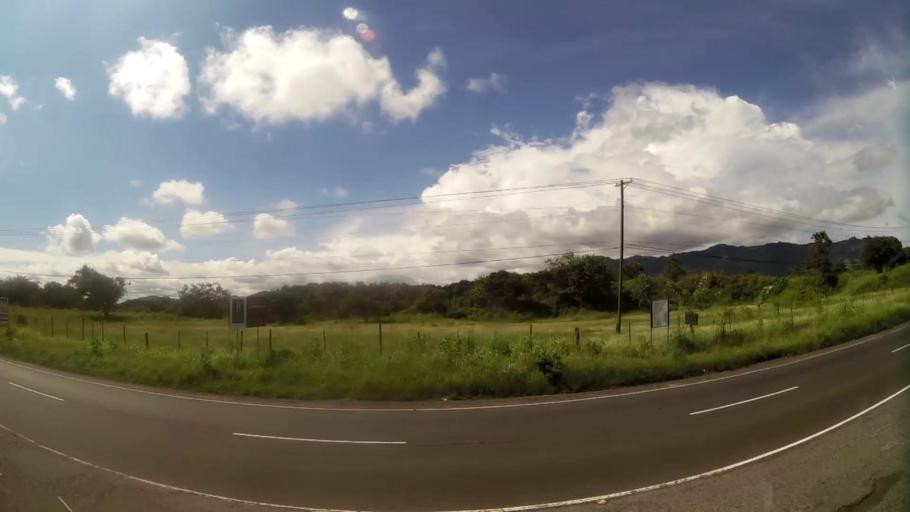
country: PA
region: Panama
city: Bejuco
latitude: 8.6134
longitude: -79.8813
